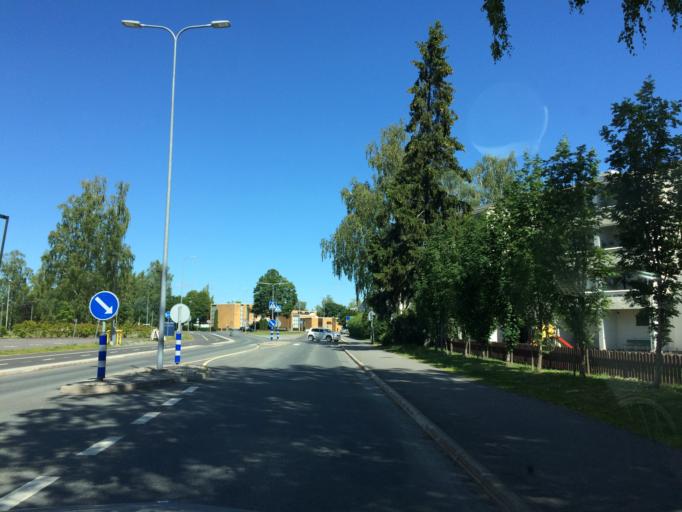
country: FI
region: Haeme
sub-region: Haemeenlinna
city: Haemeenlinna
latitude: 60.9898
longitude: 24.4396
